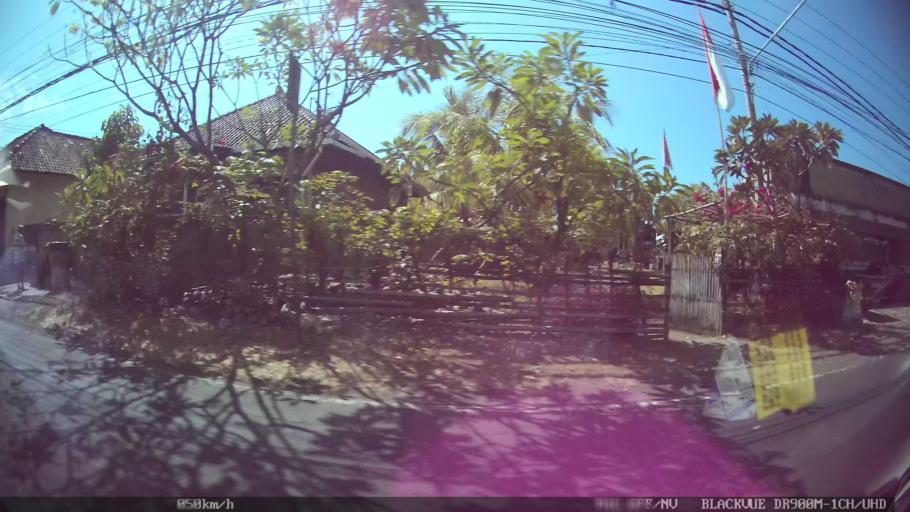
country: ID
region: Bali
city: Banjar
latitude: -8.1865
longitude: 114.9767
